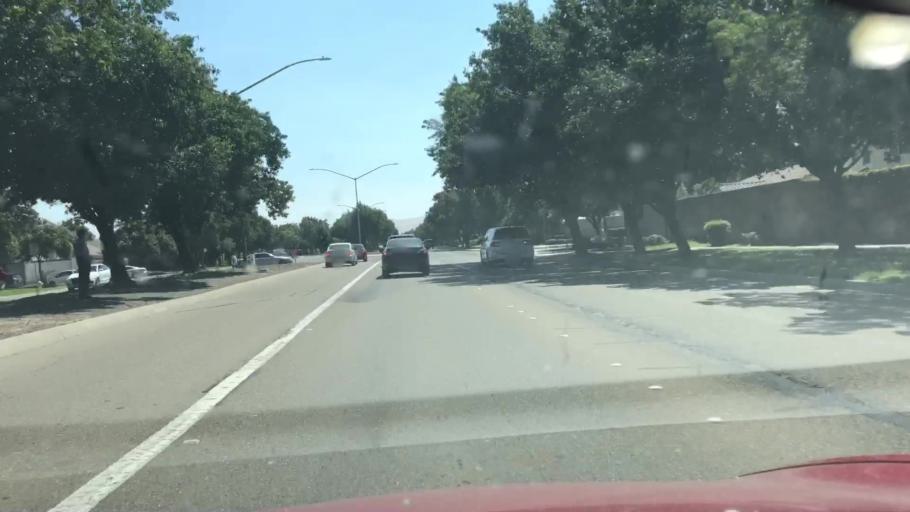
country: US
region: California
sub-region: San Joaquin County
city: Tracy
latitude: 37.7322
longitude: -121.4532
